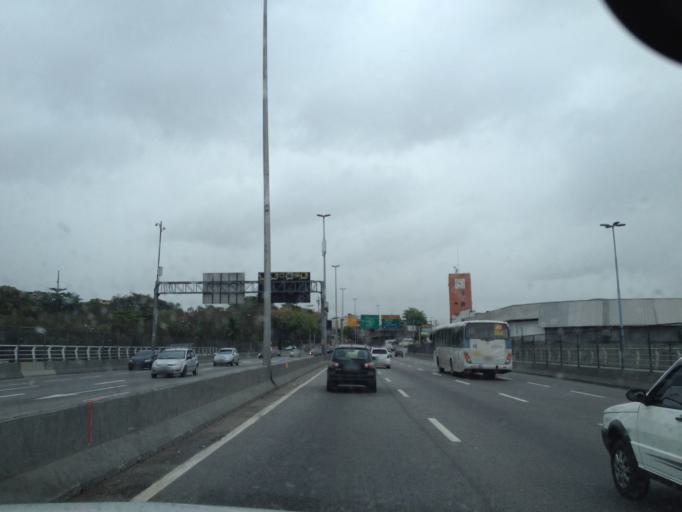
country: BR
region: Rio de Janeiro
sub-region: Rio De Janeiro
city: Rio de Janeiro
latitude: -22.8707
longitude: -43.2459
